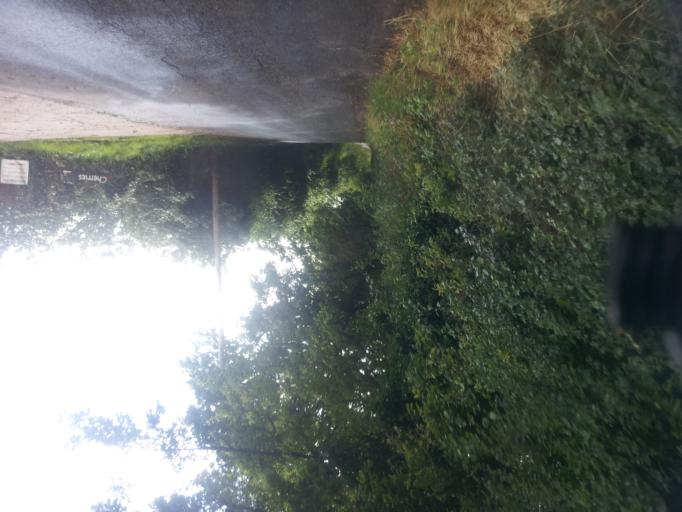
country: GB
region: England
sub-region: Kent
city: Newington
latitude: 51.3632
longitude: 0.6617
